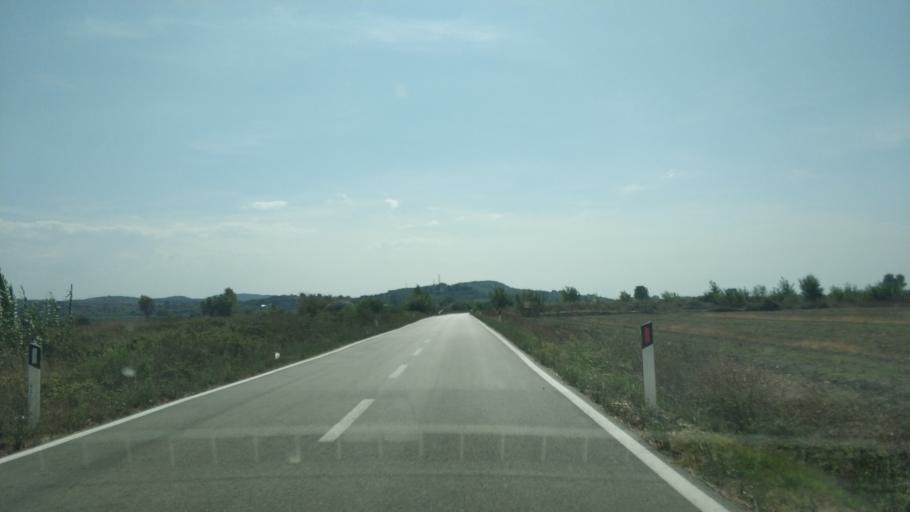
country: AL
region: Fier
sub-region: Rrethi i Fierit
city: Dermenas
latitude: 40.7458
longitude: 19.4857
